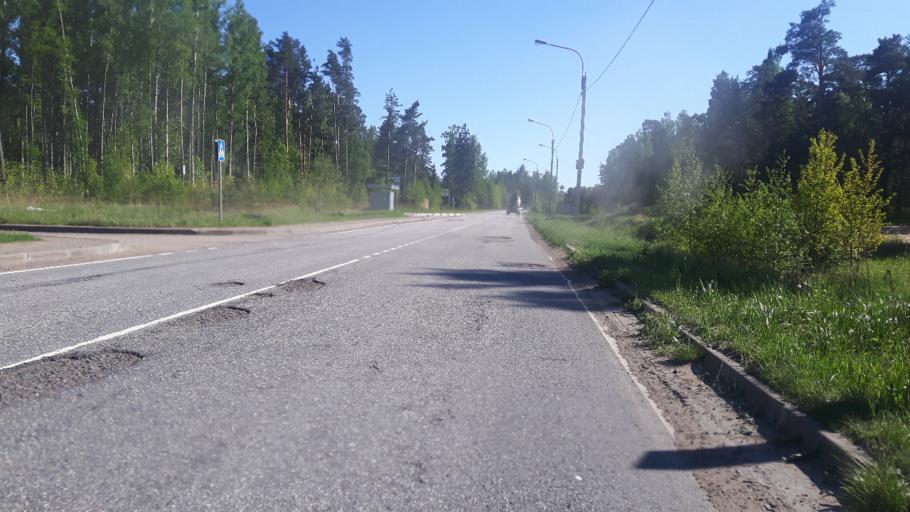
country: RU
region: Leningrad
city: Sosnovyy Bor
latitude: 60.1998
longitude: 29.0071
